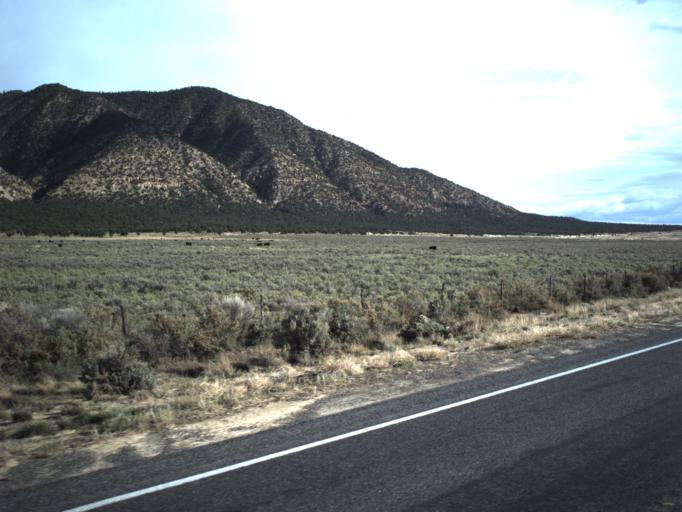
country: US
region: Utah
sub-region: Sevier County
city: Aurora
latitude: 39.0716
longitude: -112.0421
